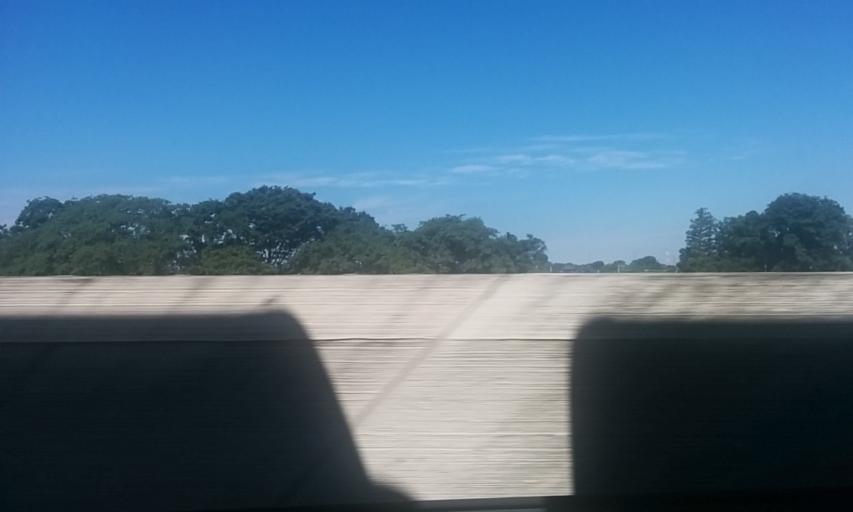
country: JP
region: Ibaraki
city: Moriya
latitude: 35.9167
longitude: 139.9592
